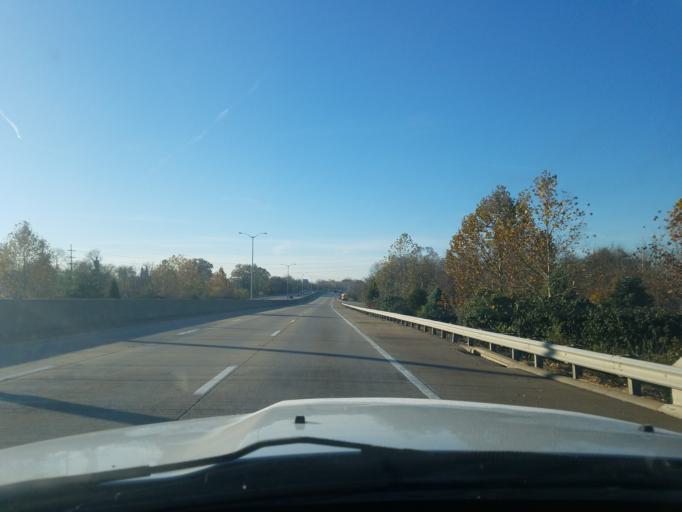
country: US
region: Indiana
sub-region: Floyd County
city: New Albany
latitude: 38.2543
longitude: -85.8060
